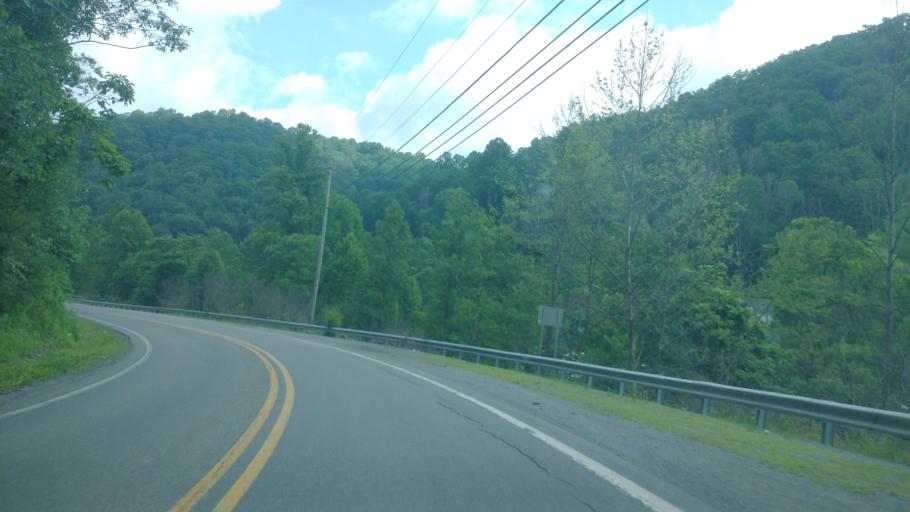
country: US
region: West Virginia
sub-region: McDowell County
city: Welch
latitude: 37.4026
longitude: -81.4190
